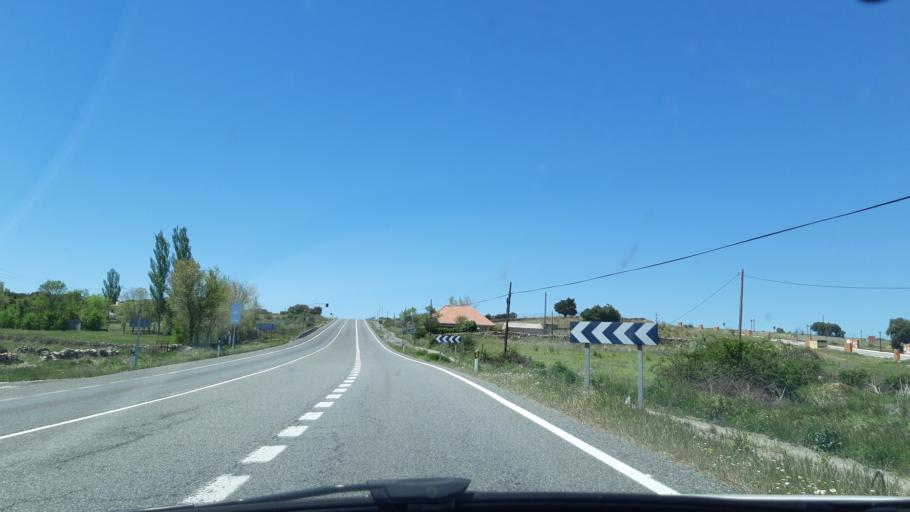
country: ES
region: Castille and Leon
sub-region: Provincia de Segovia
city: Zarzuela del Monte
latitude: 40.7589
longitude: -4.3338
